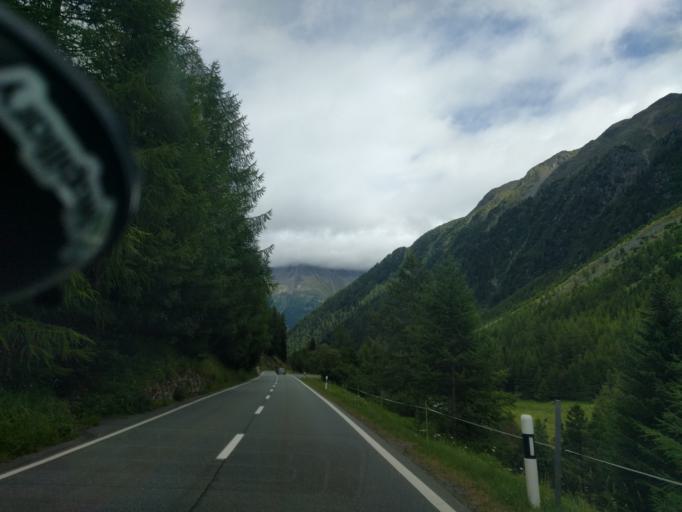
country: CH
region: Grisons
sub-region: Inn District
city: Zernez
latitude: 46.7528
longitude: 10.0378
